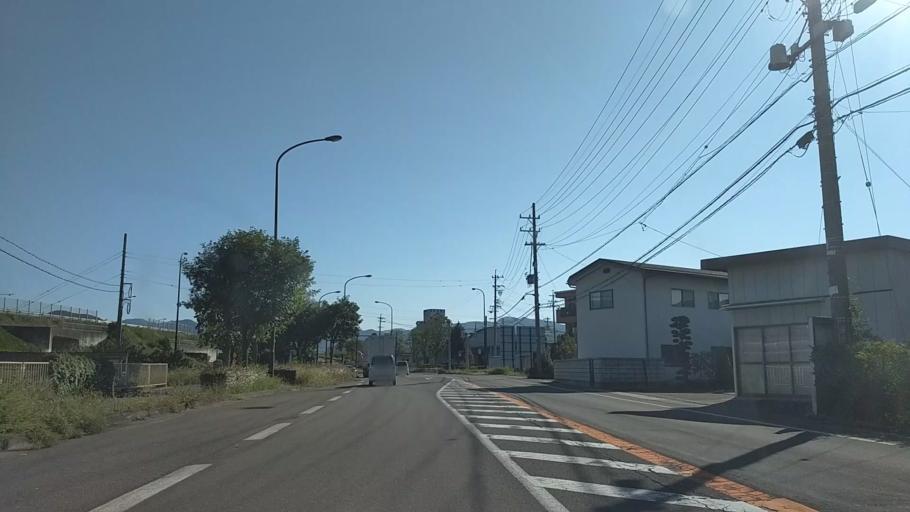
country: JP
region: Nagano
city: Nagano-shi
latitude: 36.5633
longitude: 138.1388
